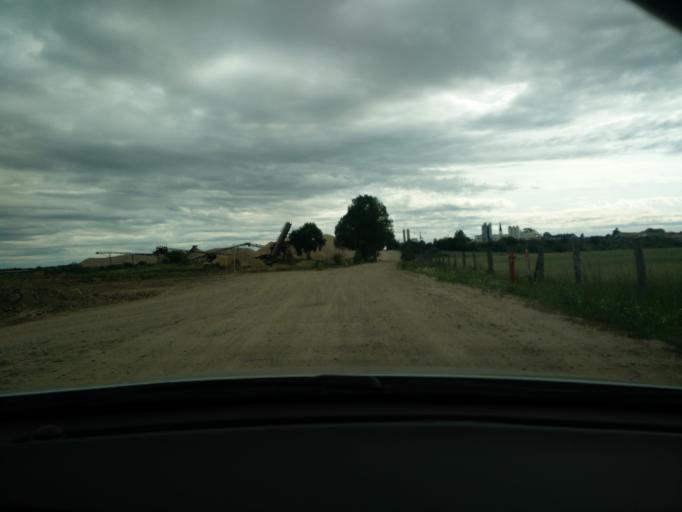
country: PL
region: Pomeranian Voivodeship
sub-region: Powiat pucki
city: Mrzezino
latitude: 54.6575
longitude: 18.4397
